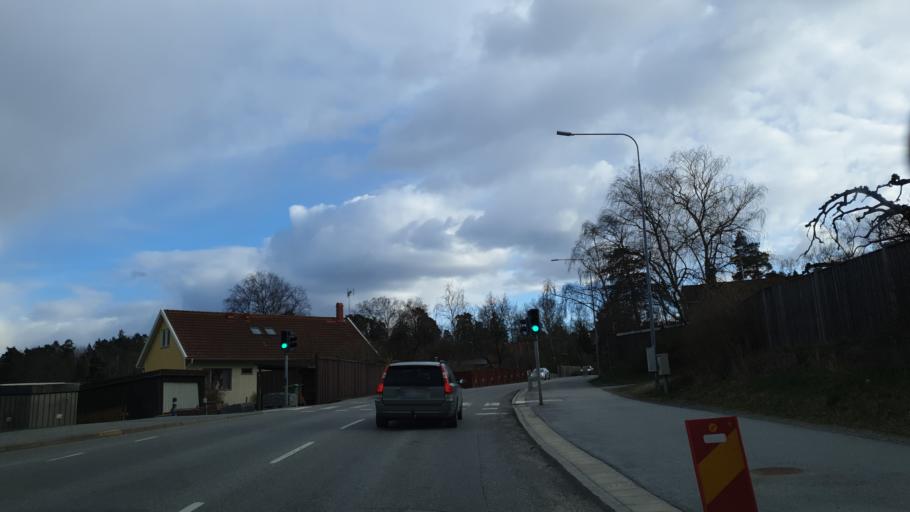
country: SE
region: Stockholm
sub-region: Lidingo
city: Lidingoe
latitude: 59.3729
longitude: 18.1331
